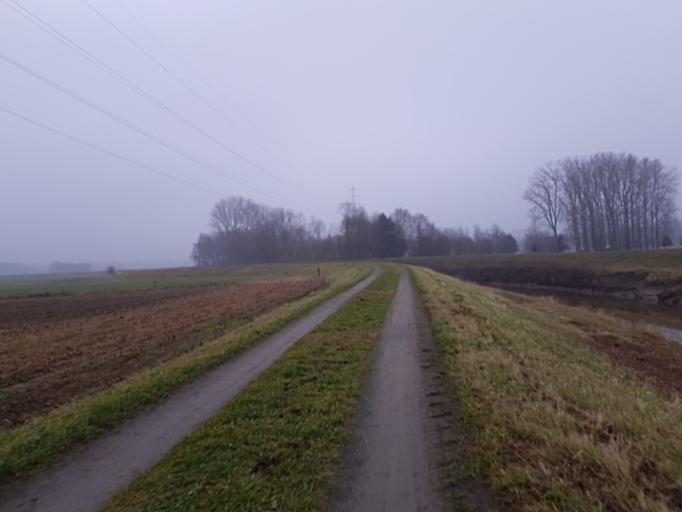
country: BE
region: Flanders
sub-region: Provincie Vlaams-Brabant
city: Keerbergen
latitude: 50.9931
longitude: 4.6262
